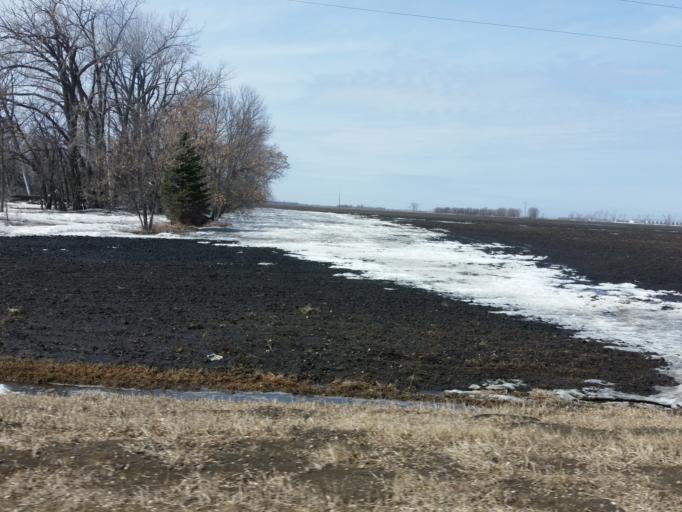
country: US
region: North Dakota
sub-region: Walsh County
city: Grafton
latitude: 48.2826
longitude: -97.2546
